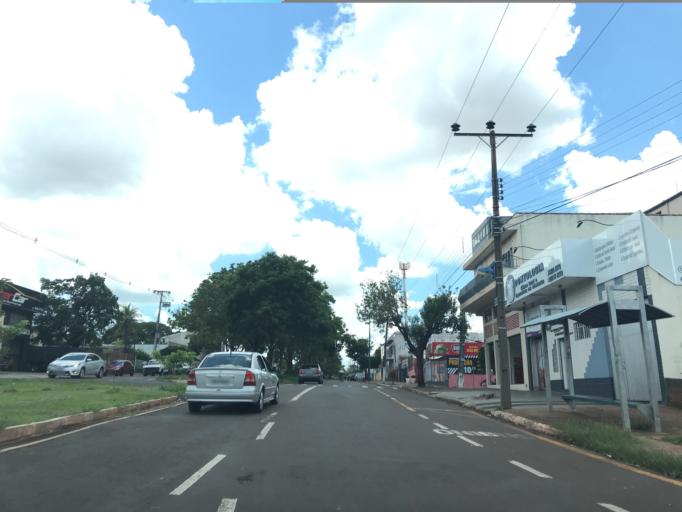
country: BR
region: Parana
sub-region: Maringa
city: Maringa
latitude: -23.3906
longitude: -51.9162
